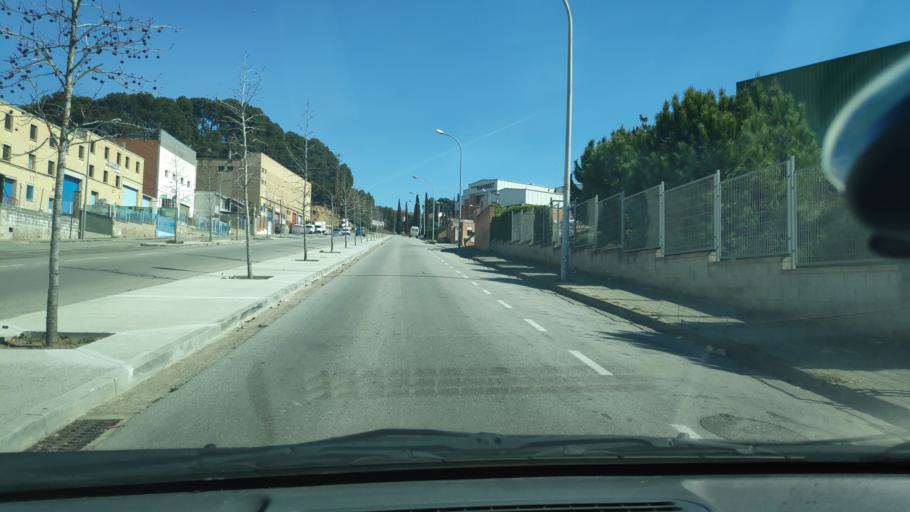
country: ES
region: Catalonia
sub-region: Provincia de Barcelona
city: Rubi
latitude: 41.5046
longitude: 2.0434
